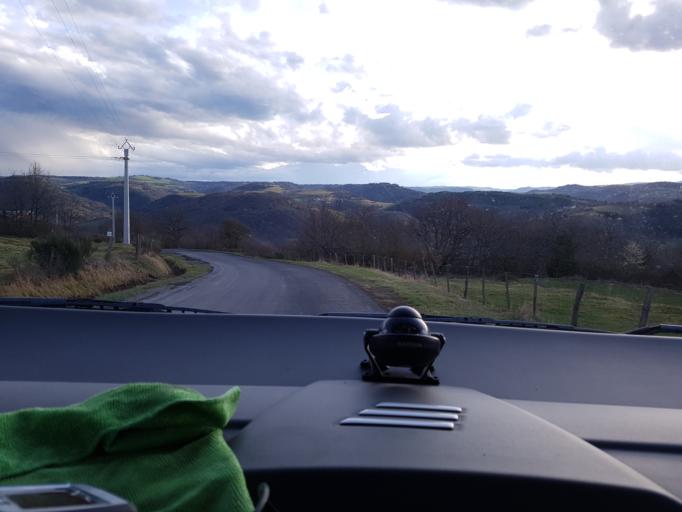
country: FR
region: Auvergne
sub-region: Departement du Cantal
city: Massiac
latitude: 45.2929
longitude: 3.1985
